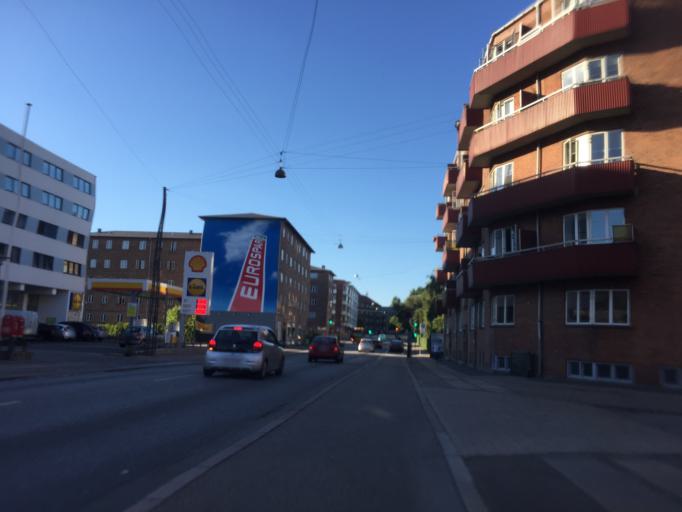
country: DK
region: Capital Region
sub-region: Frederiksberg Kommune
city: Frederiksberg
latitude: 55.6674
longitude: 12.5173
